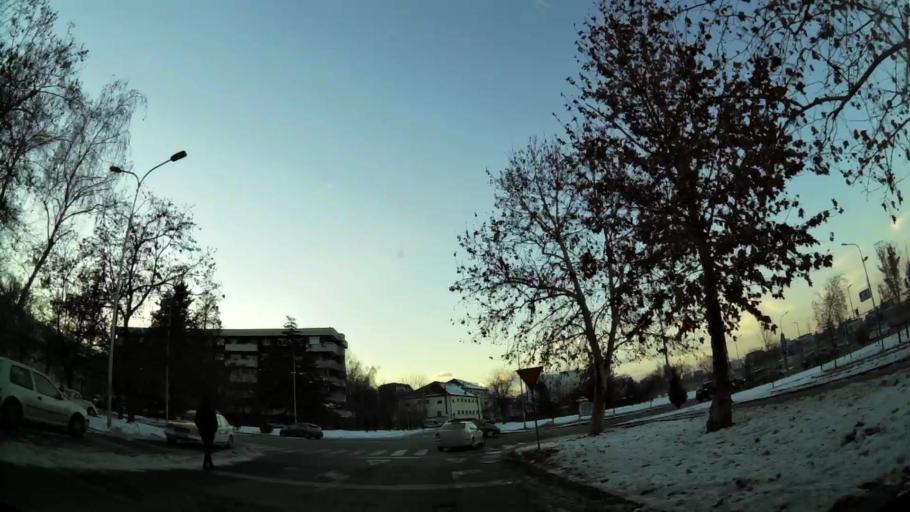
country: MK
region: Karpos
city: Skopje
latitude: 41.9957
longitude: 21.4037
